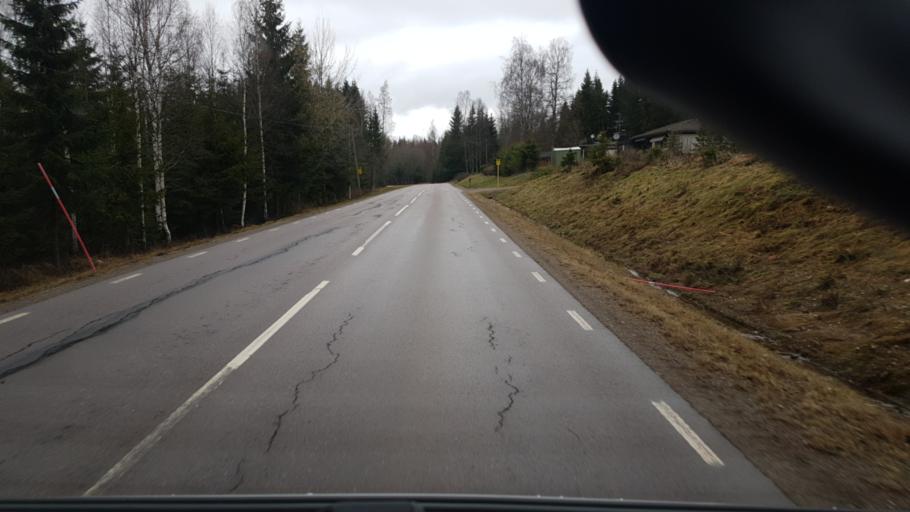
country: SE
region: Vaermland
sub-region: Eda Kommun
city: Charlottenberg
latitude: 59.9003
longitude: 12.3005
